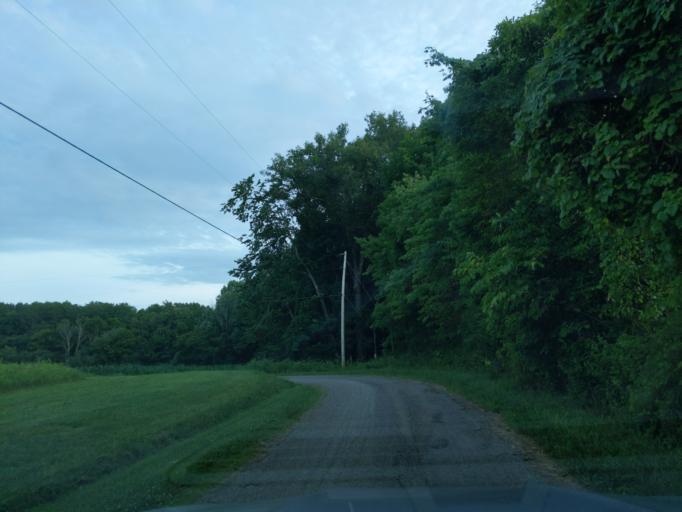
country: US
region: Indiana
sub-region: Ripley County
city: Sunman
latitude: 39.3105
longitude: -85.0997
